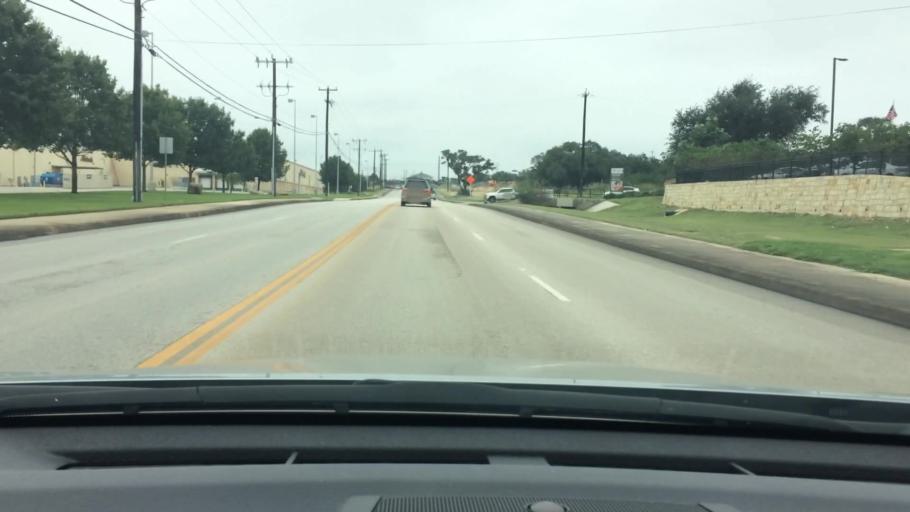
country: US
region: Texas
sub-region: Bexar County
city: Helotes
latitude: 29.4914
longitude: -98.7120
